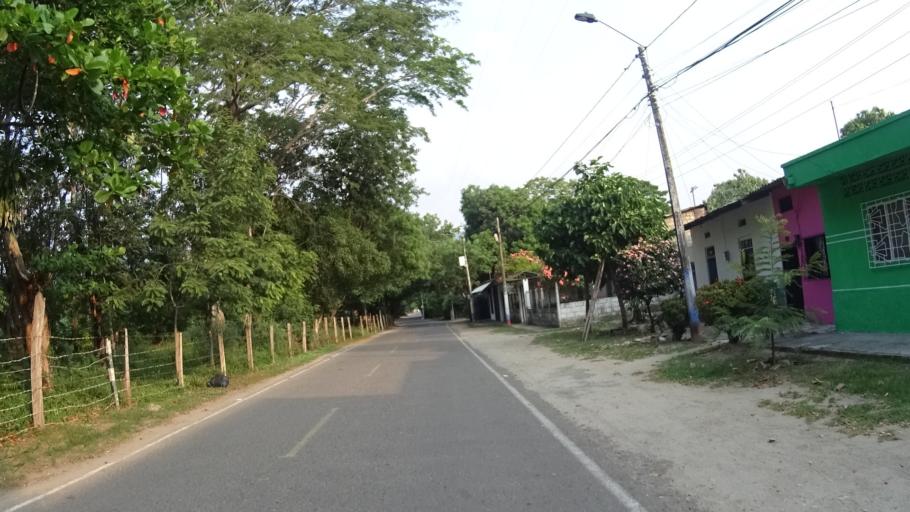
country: CO
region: Caldas
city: La Dorada
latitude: 5.4471
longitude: -74.6592
